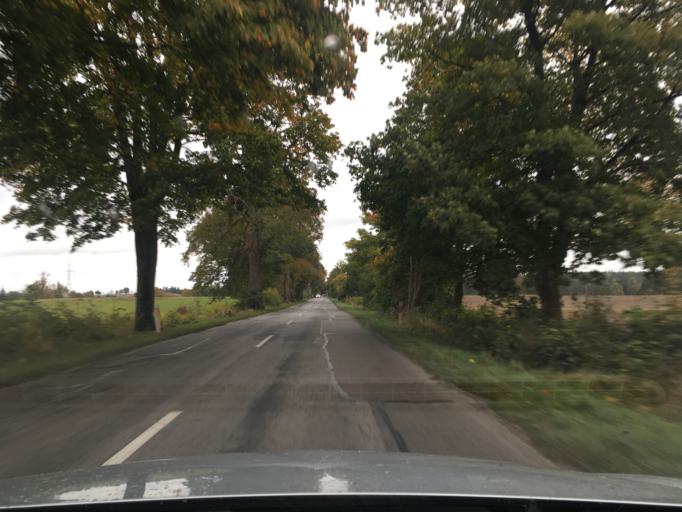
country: PL
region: Pomeranian Voivodeship
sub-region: Powiat koscierski
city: Grabowo Koscierskie
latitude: 54.1195
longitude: 18.1382
